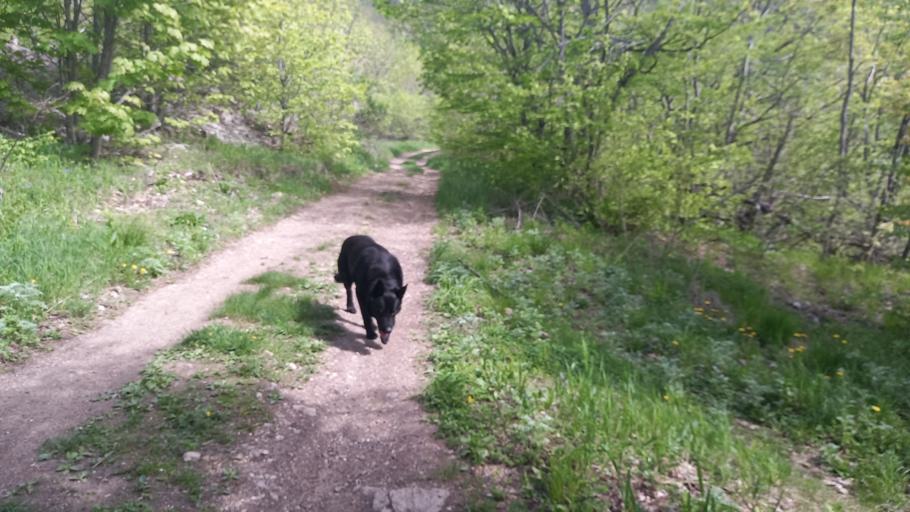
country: RU
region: Stavropol'skiy
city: Pyatigorsk
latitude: 44.0892
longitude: 43.0296
